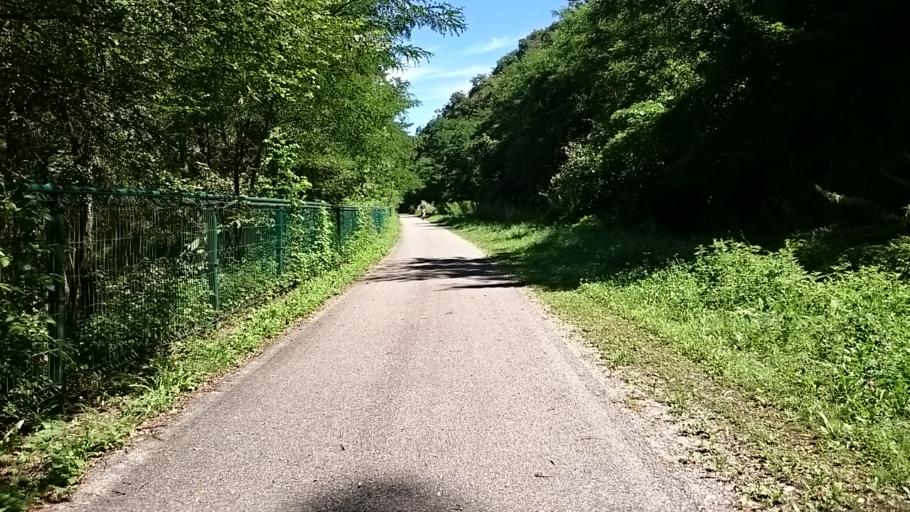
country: IT
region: Trentino-Alto Adige
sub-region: Bolzano
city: Collalbo
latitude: 46.5079
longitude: 11.4672
